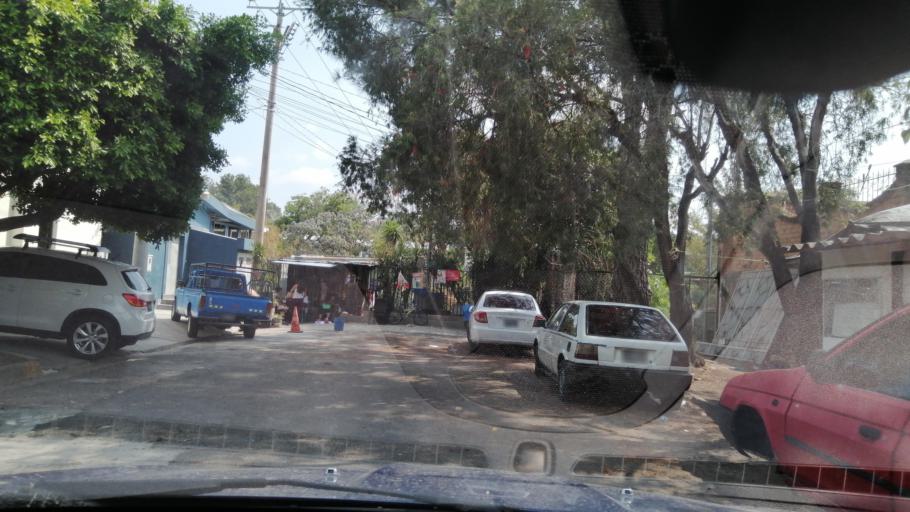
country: SV
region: La Libertad
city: Antiguo Cuscatlan
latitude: 13.7007
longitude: -89.2401
